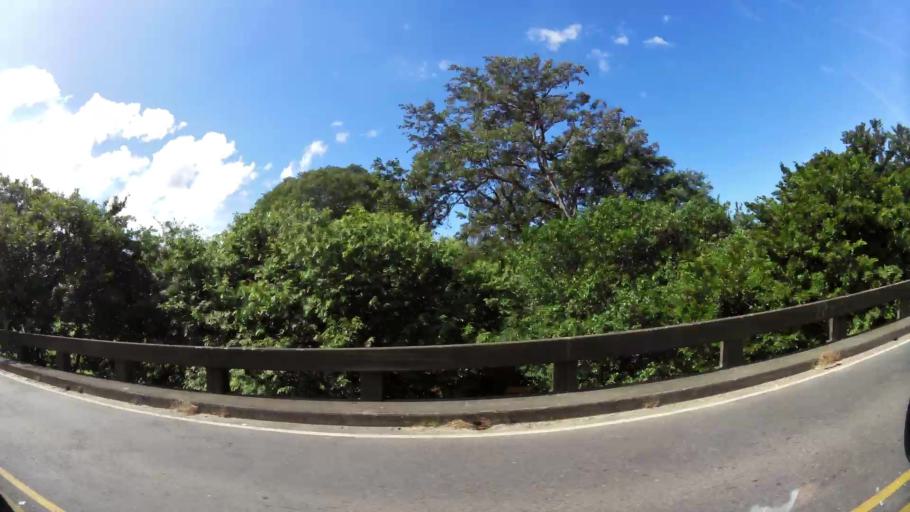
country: CR
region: Guanacaste
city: Juntas
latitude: 10.3214
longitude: -85.0470
